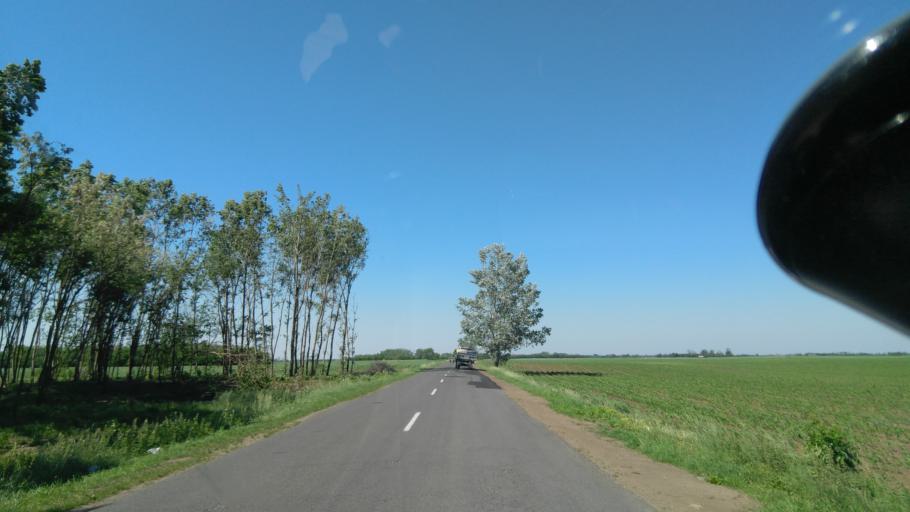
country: HU
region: Bekes
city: Kevermes
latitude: 46.4356
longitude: 21.1748
